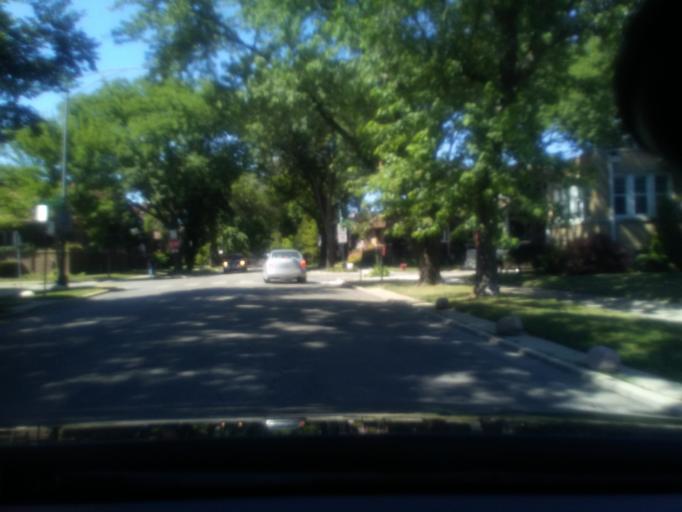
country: US
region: Illinois
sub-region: Cook County
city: Lincolnwood
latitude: 41.9705
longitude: -87.6988
